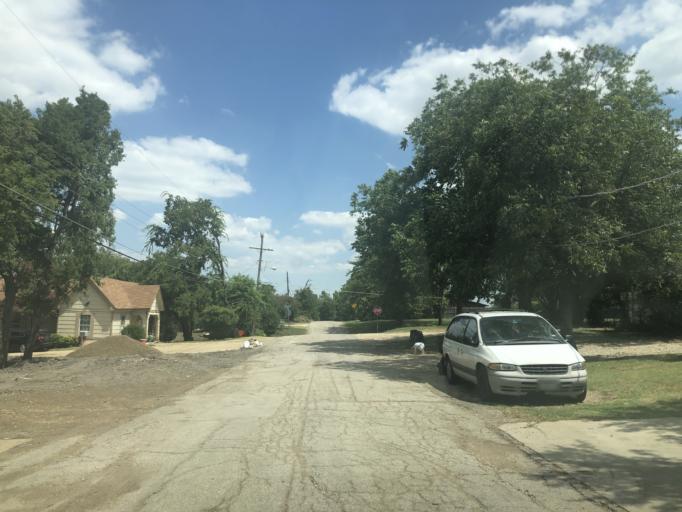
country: US
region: Texas
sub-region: Dallas County
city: Grand Prairie
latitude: 32.7468
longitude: -97.0278
